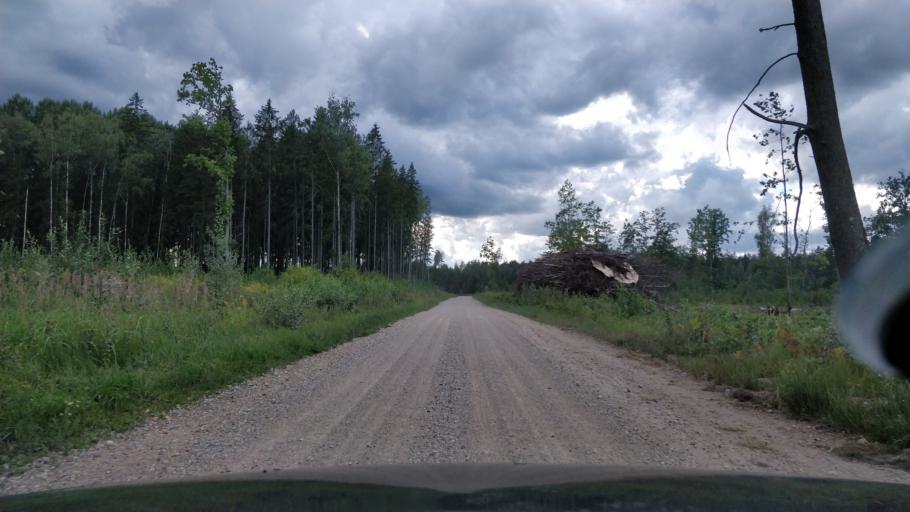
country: LV
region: Kegums
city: Kegums
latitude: 56.8061
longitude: 24.6952
